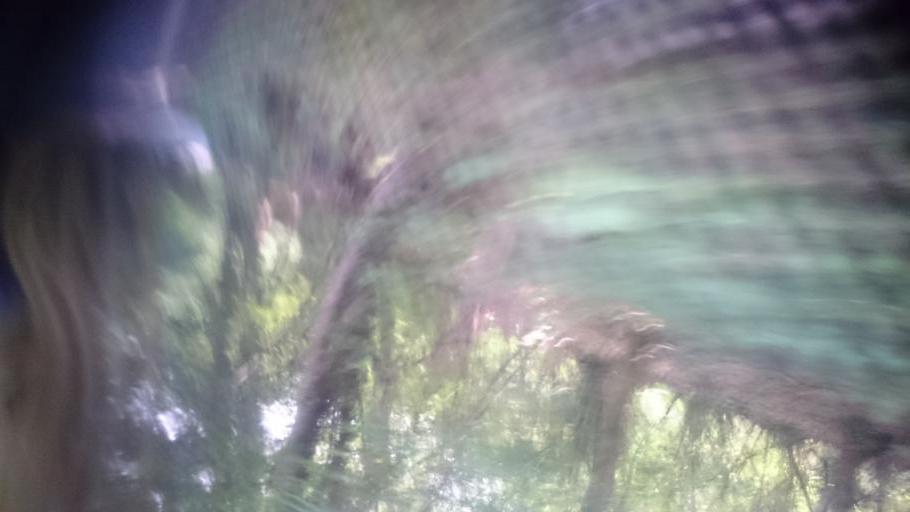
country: ES
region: Asturias
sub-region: Province of Asturias
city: Amieva
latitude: 43.3002
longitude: -5.0368
